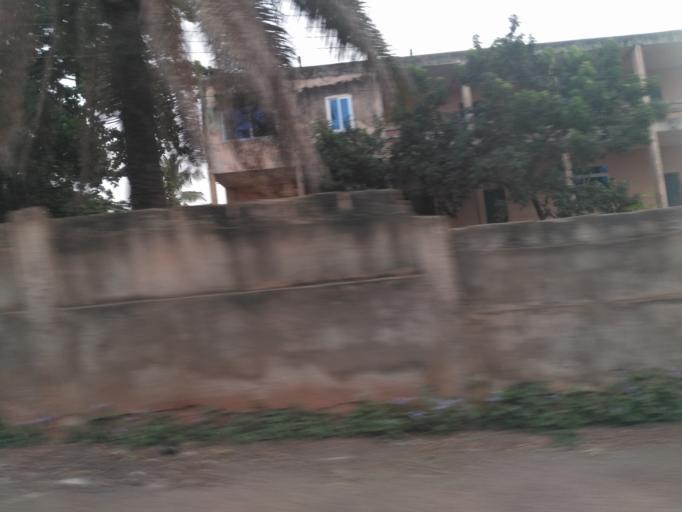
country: GH
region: Ashanti
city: Kumasi
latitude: 6.6841
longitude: -1.6202
